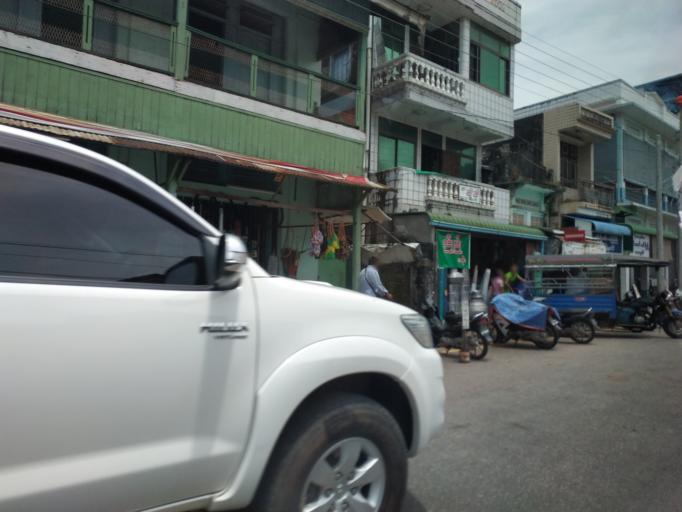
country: MM
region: Tanintharyi
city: Dawei
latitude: 14.0730
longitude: 98.1909
